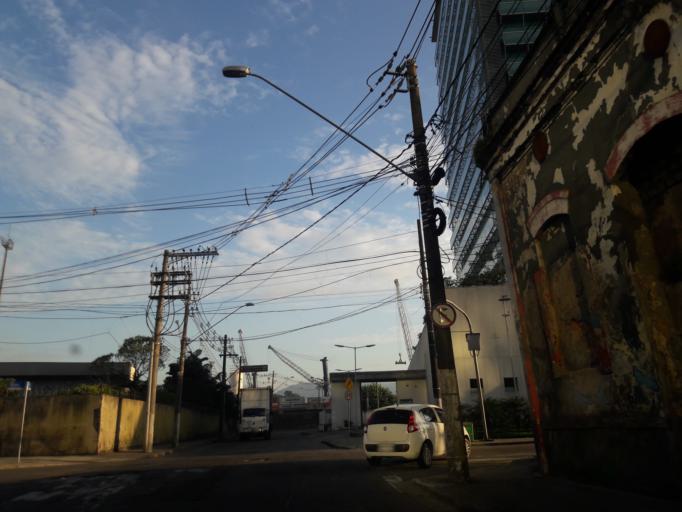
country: BR
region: Sao Paulo
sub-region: Santos
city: Santos
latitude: -23.9308
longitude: -46.3369
